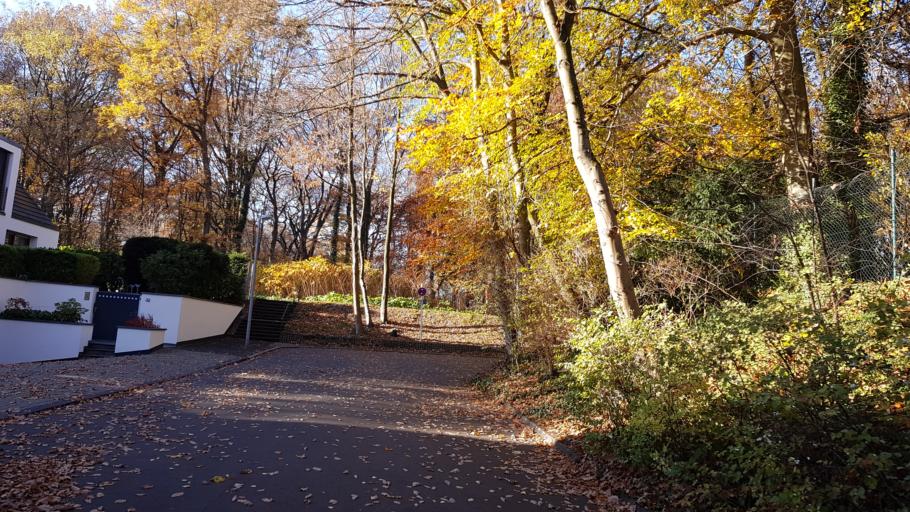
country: DE
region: North Rhine-Westphalia
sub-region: Regierungsbezirk Dusseldorf
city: Duisburg
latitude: 51.4304
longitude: 6.8191
